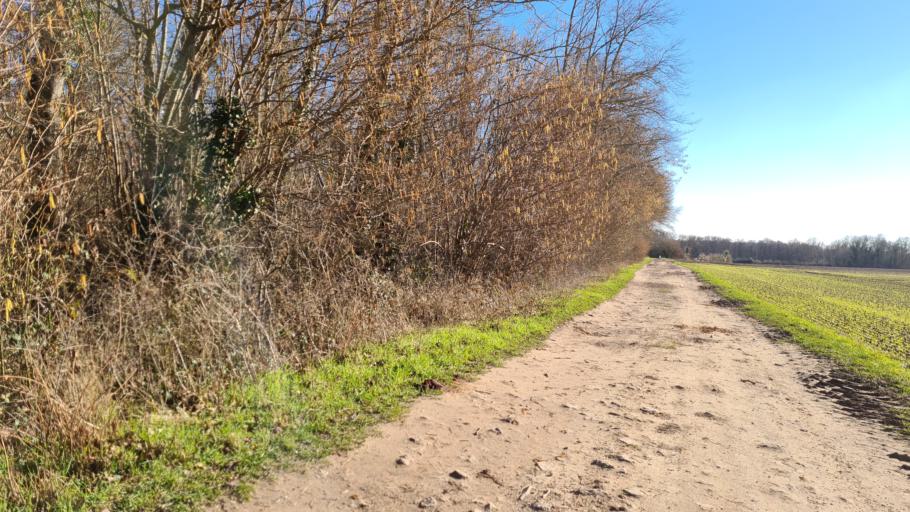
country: FR
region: Picardie
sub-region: Departement de l'Aisne
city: Athies-sous-Laon
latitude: 49.5576
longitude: 3.6559
